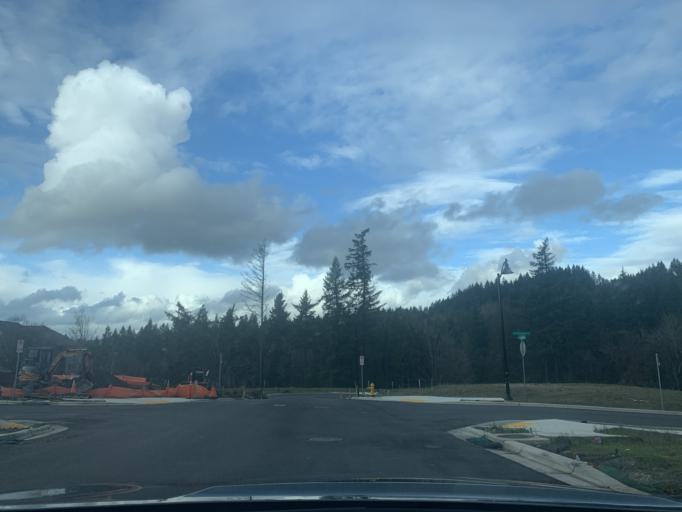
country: US
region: Oregon
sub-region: Washington County
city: Cedar Mill
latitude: 45.5520
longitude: -122.8050
